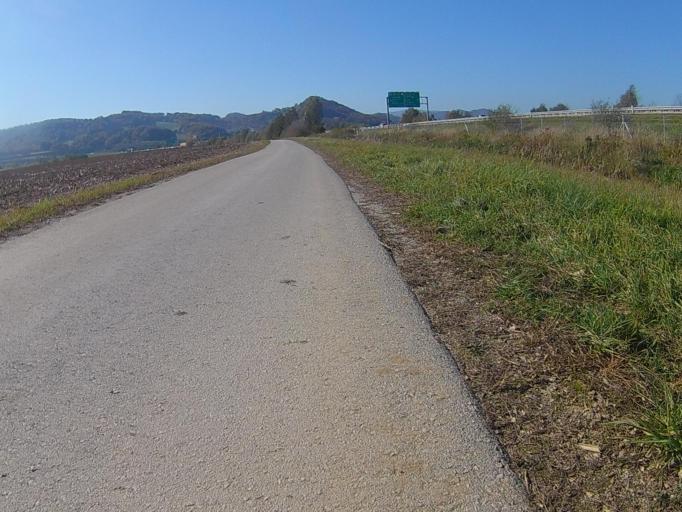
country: SI
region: Pesnica
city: Pesnica pri Mariboru
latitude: 46.5931
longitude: 15.6995
